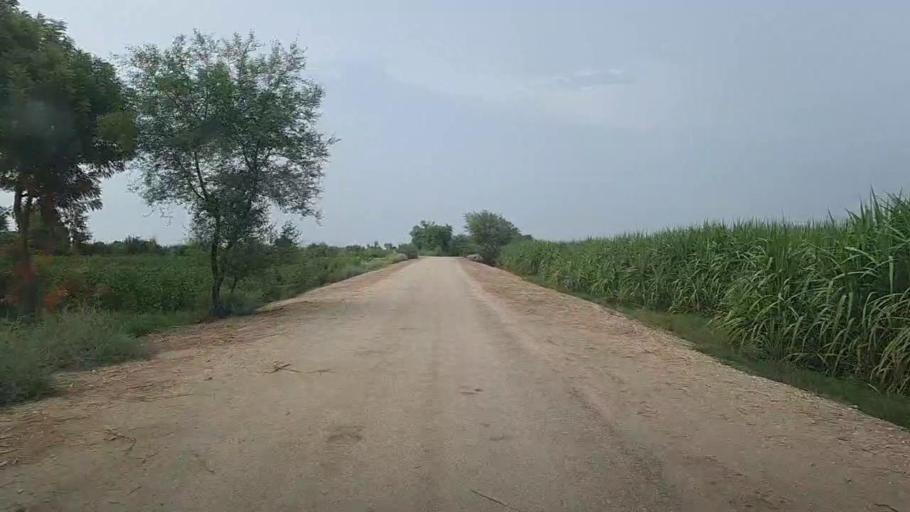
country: PK
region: Sindh
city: Karaundi
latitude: 26.9758
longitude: 68.4288
